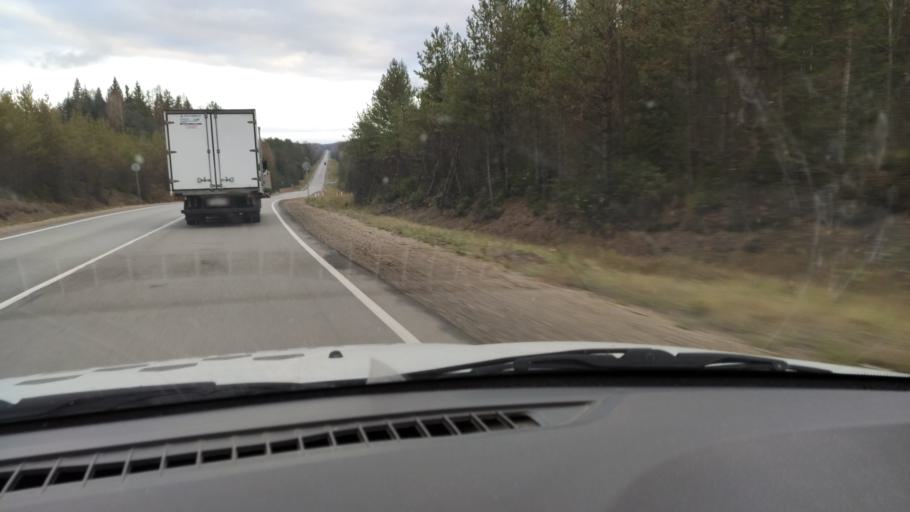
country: RU
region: Kirov
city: Chernaya Kholunitsa
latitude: 58.8504
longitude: 51.7408
